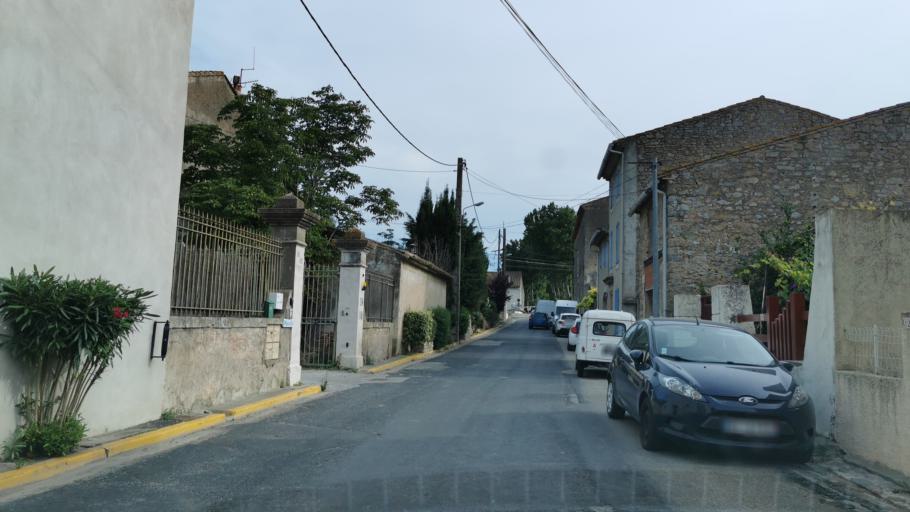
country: FR
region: Languedoc-Roussillon
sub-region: Departement de l'Aude
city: Nevian
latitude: 43.2110
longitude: 2.9044
